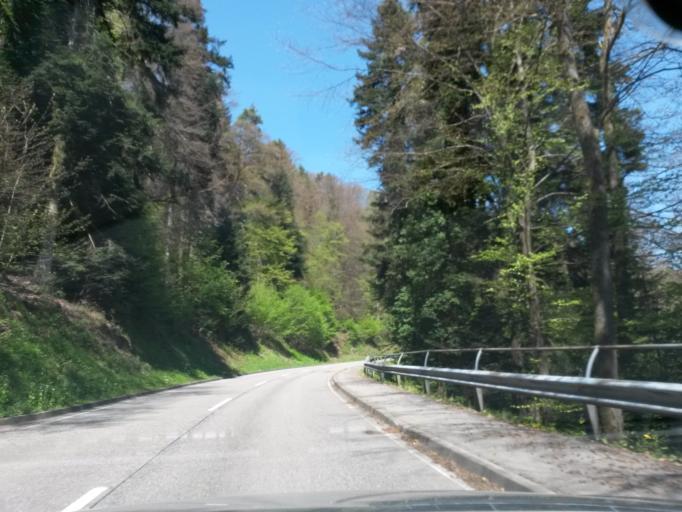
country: DE
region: Baden-Wuerttemberg
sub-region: Karlsruhe Region
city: Birkenfeld
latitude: 48.8638
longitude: 8.6371
